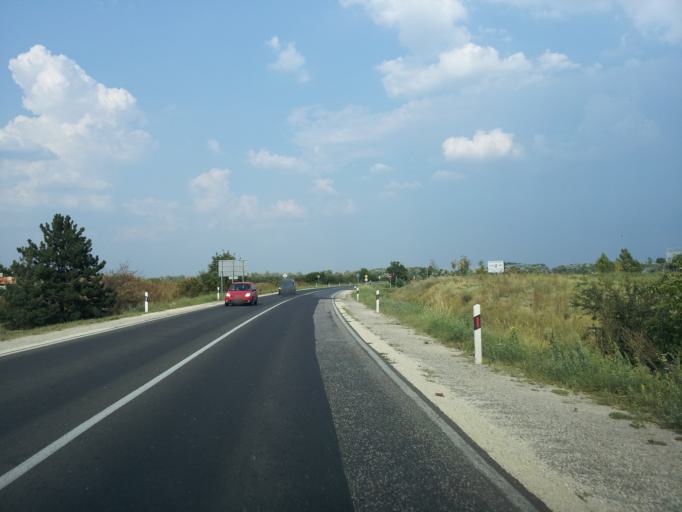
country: HU
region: Pest
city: Taksony
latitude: 47.3095
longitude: 19.0413
